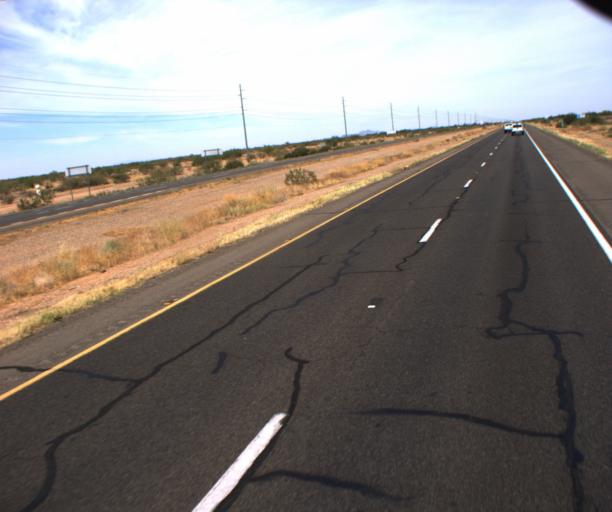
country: US
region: Arizona
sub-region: Maricopa County
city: Sun City West
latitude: 33.7149
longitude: -112.4477
